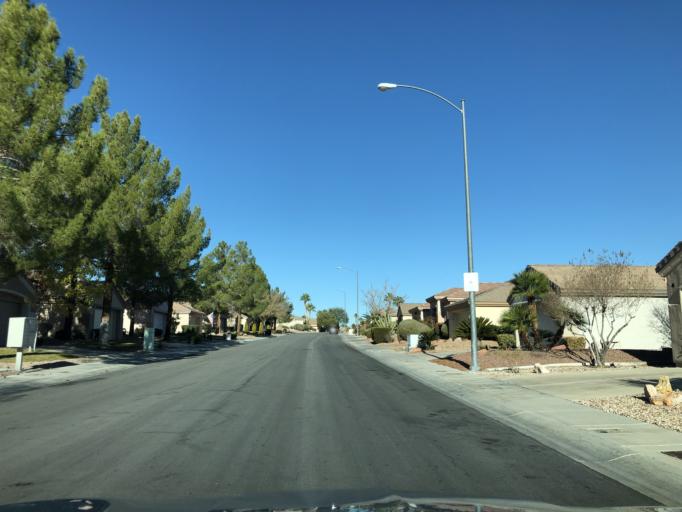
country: US
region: Nevada
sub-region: Clark County
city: Whitney
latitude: 36.0063
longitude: -115.0720
